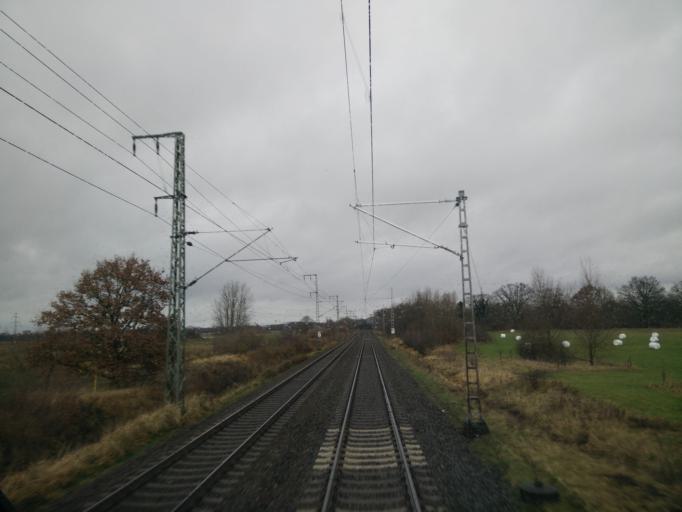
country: DE
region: Mecklenburg-Vorpommern
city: Klein Rogahn
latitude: 53.5810
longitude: 11.3808
